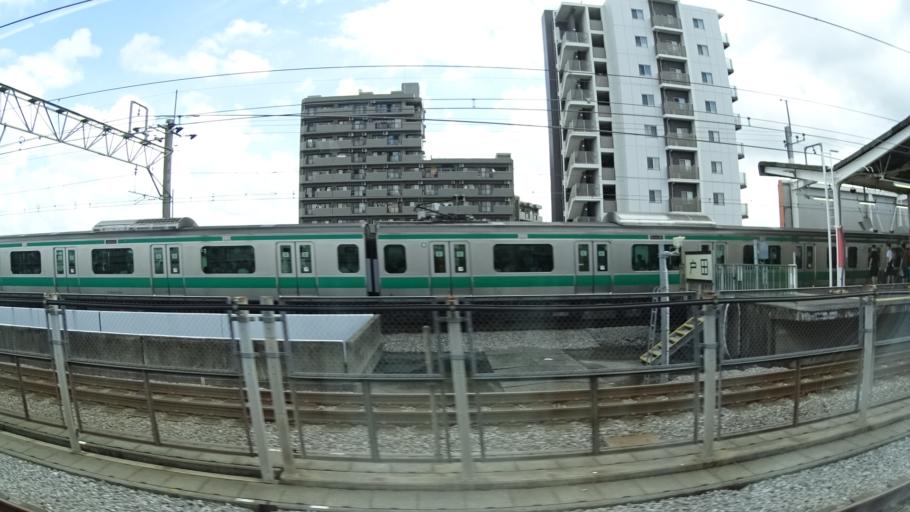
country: JP
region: Saitama
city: Shimotoda
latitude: 35.8220
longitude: 139.6669
